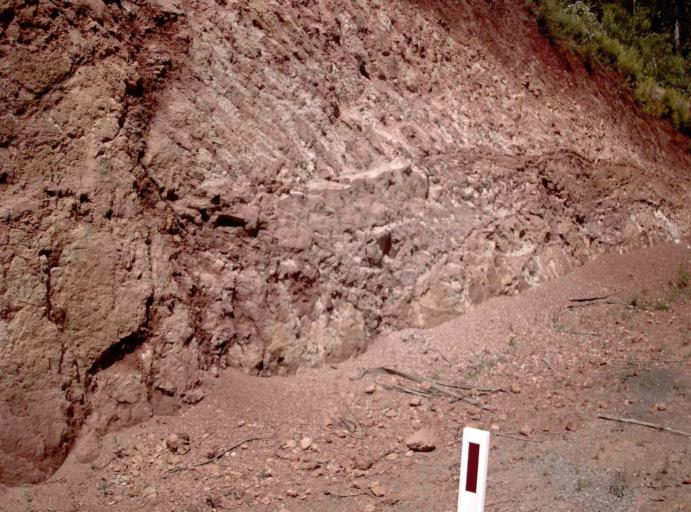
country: AU
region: Victoria
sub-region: Latrobe
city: Traralgon
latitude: -38.3327
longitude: 146.5719
